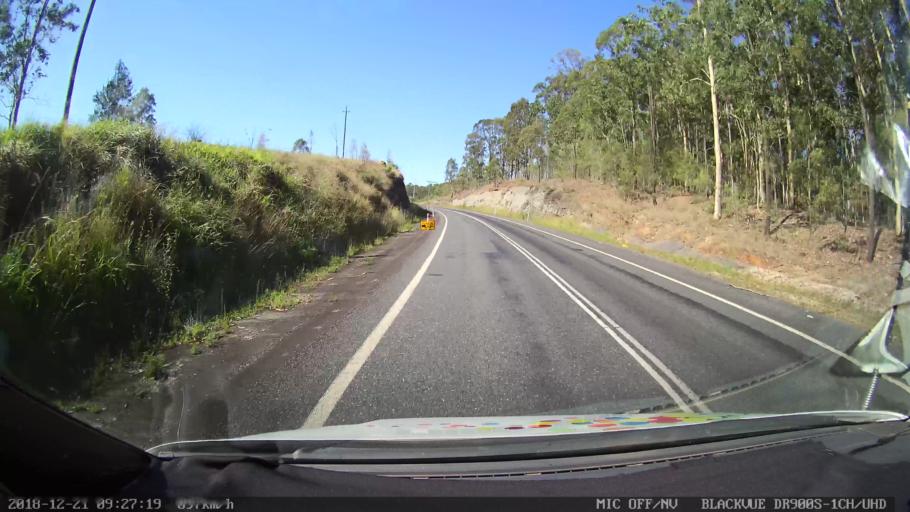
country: AU
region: New South Wales
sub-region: Clarence Valley
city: Maclean
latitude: -29.4011
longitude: 152.9908
